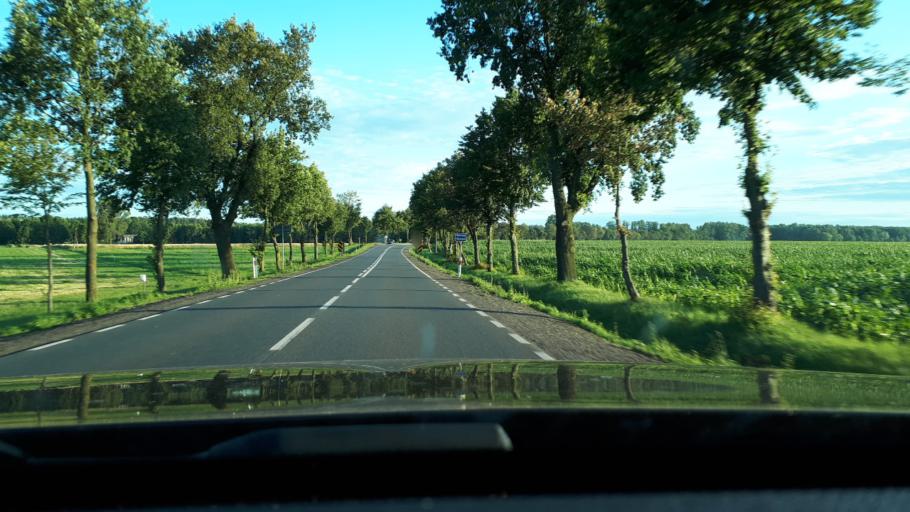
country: PL
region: Masovian Voivodeship
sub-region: Powiat ciechanowski
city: Ciechanow
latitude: 52.8110
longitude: 20.6076
